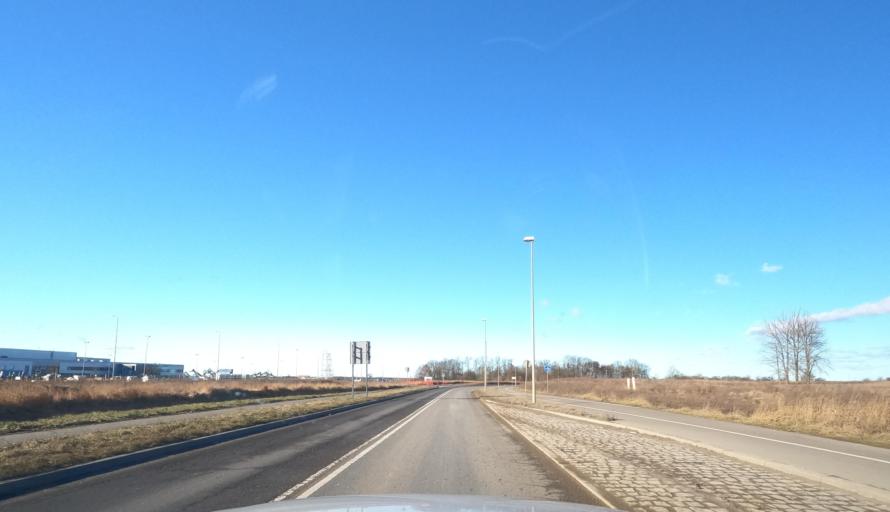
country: PL
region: West Pomeranian Voivodeship
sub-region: Powiat pyrzycki
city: Warnice
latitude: 53.2924
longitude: 14.9599
